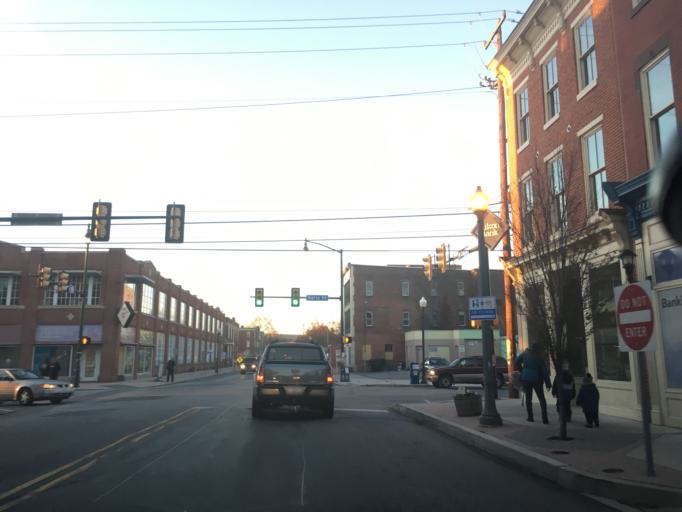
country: US
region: Pennsylvania
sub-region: Dauphin County
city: Harrisburg
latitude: 40.2713
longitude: -76.8902
